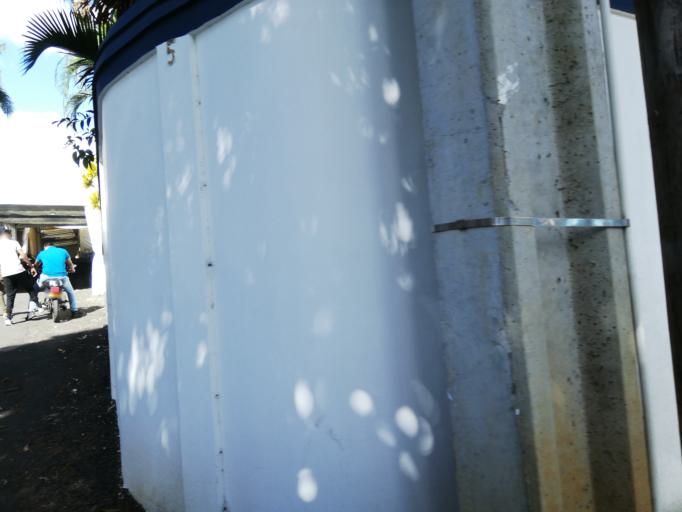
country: MU
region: Moka
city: Moka
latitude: -20.2273
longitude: 57.4758
